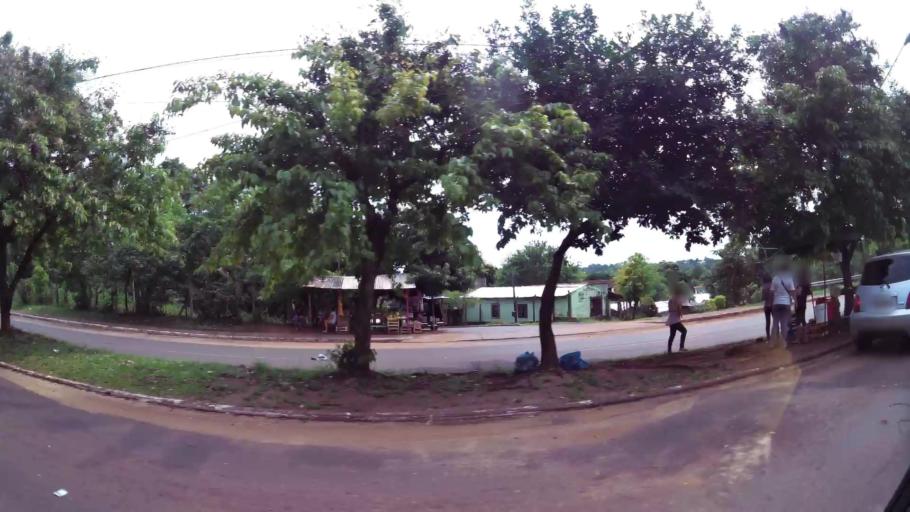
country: PY
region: Alto Parana
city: Presidente Franco
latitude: -25.5495
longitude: -54.6096
